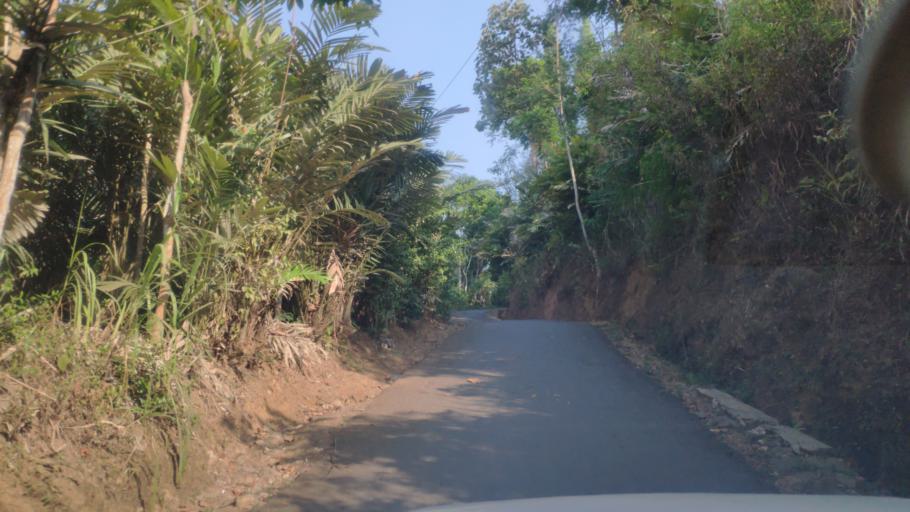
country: ID
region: Central Java
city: Wonosobo
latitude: -7.4199
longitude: 109.7386
